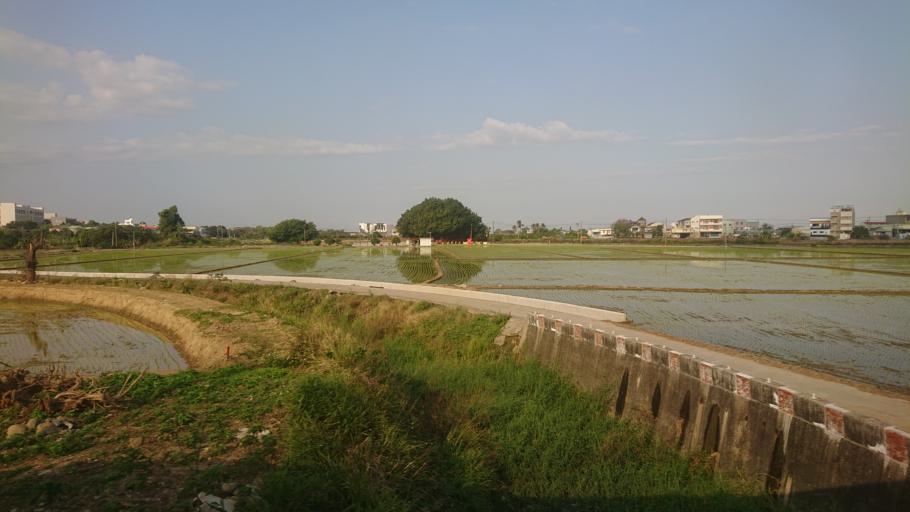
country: TW
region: Taiwan
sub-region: Chiayi
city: Jiayi Shi
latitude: 23.5470
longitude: 120.4293
